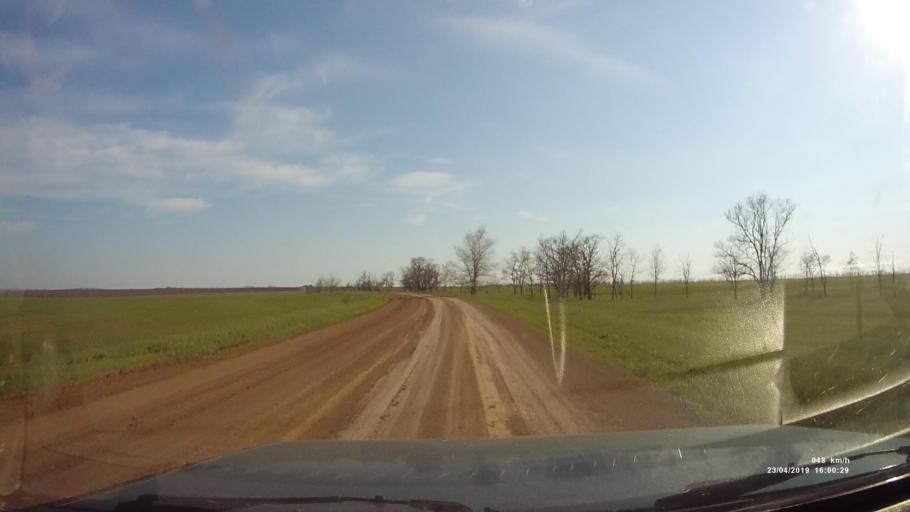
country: RU
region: Rostov
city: Remontnoye
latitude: 46.5094
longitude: 43.1075
